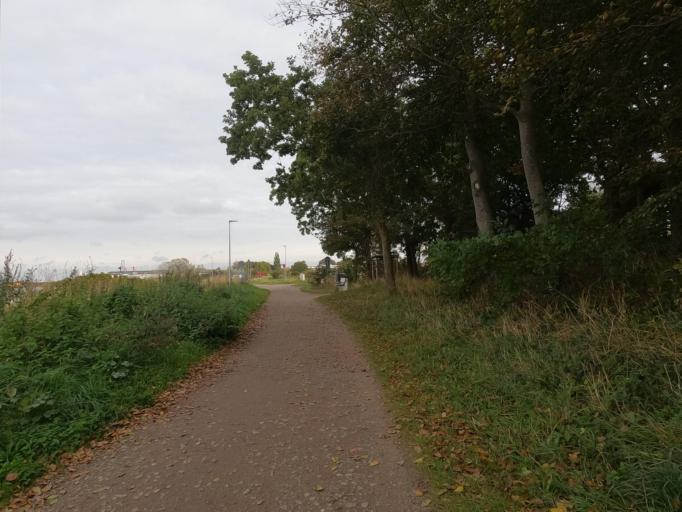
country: DE
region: Schleswig-Holstein
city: Heiligenhafen
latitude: 54.3695
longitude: 10.9999
